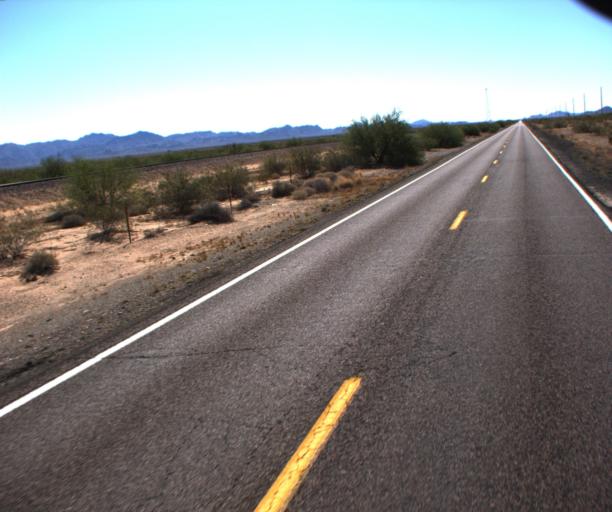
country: US
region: Arizona
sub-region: La Paz County
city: Salome
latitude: 33.8461
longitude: -113.8976
